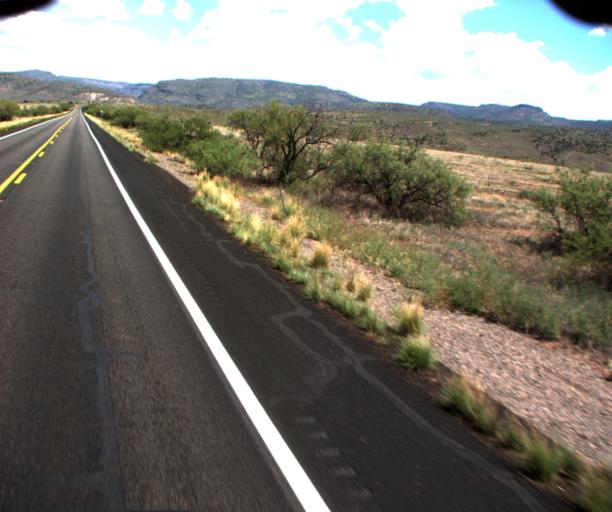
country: US
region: Arizona
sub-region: Yavapai County
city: Camp Verde
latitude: 34.5068
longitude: -111.7576
